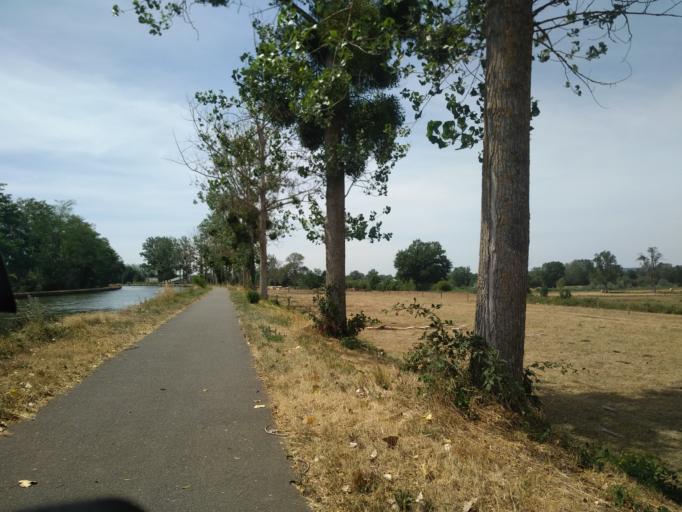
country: FR
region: Auvergne
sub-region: Departement de l'Allier
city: Molinet
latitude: 46.4796
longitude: 3.9004
